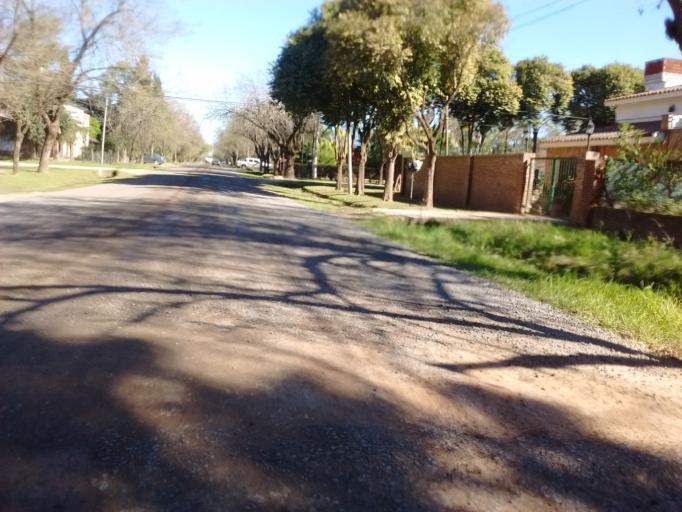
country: AR
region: Santa Fe
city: Funes
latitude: -32.9239
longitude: -60.8153
